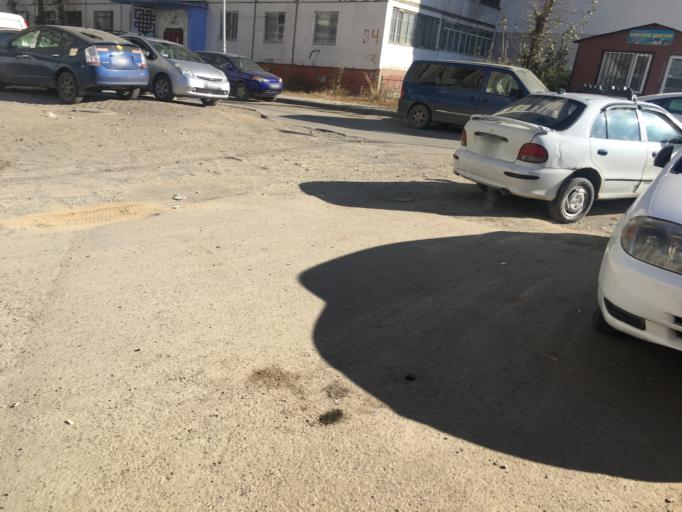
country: MN
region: Ulaanbaatar
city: Ulaanbaatar
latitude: 47.9211
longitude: 106.8880
